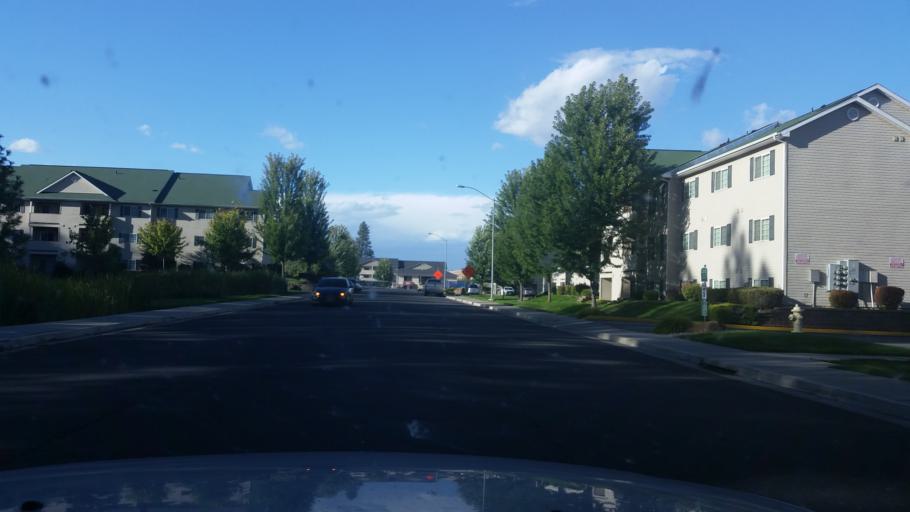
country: US
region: Washington
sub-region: Spokane County
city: Cheney
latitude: 47.5055
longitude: -117.5689
